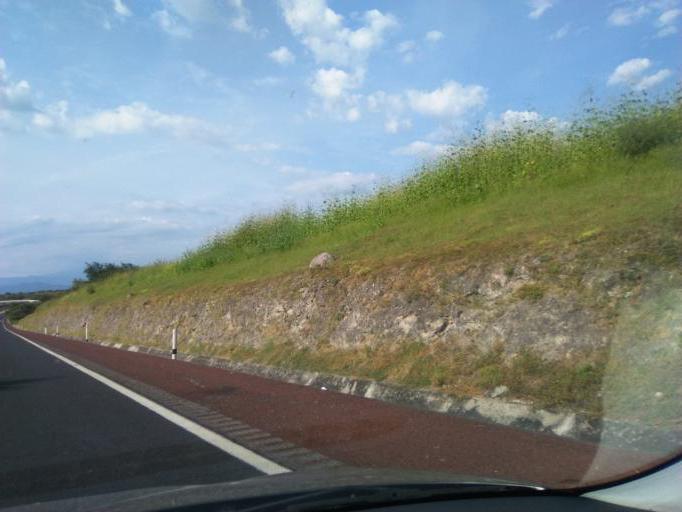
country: MX
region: Morelos
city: Puente de Ixtla
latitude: 18.6312
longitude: -99.2937
